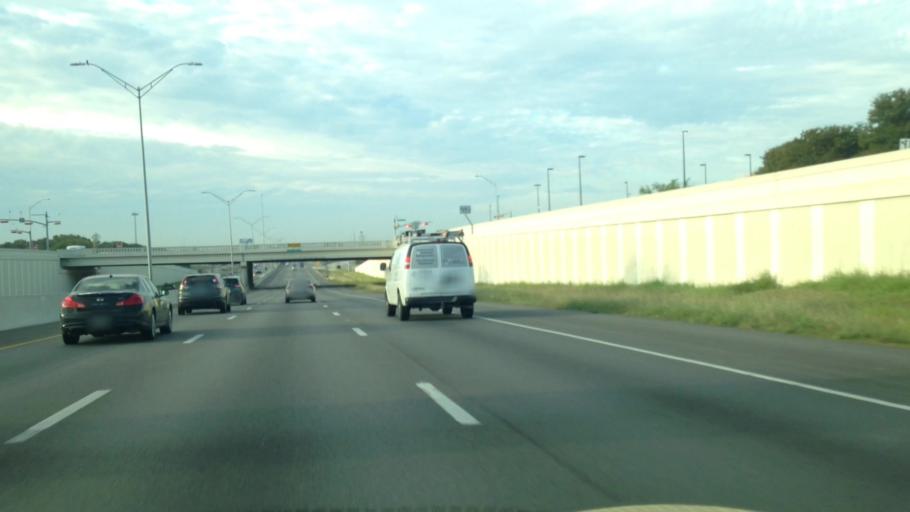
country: US
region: Texas
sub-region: Bexar County
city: Kirby
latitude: 29.4631
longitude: -98.4101
